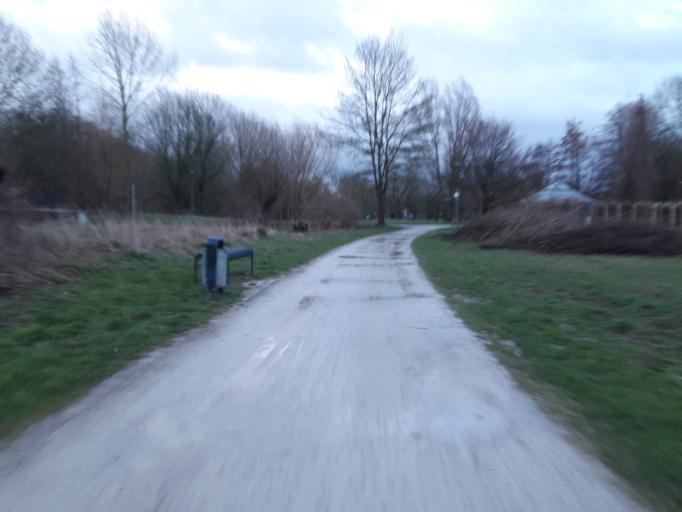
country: DE
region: North Rhine-Westphalia
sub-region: Regierungsbezirk Detmold
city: Paderborn
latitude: 51.7479
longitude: 8.7065
